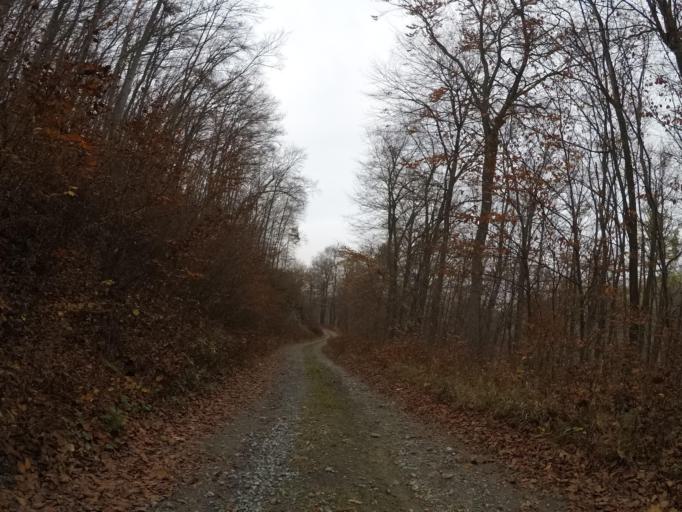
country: SK
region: Presovsky
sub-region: Okres Presov
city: Presov
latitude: 48.8967
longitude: 21.1961
